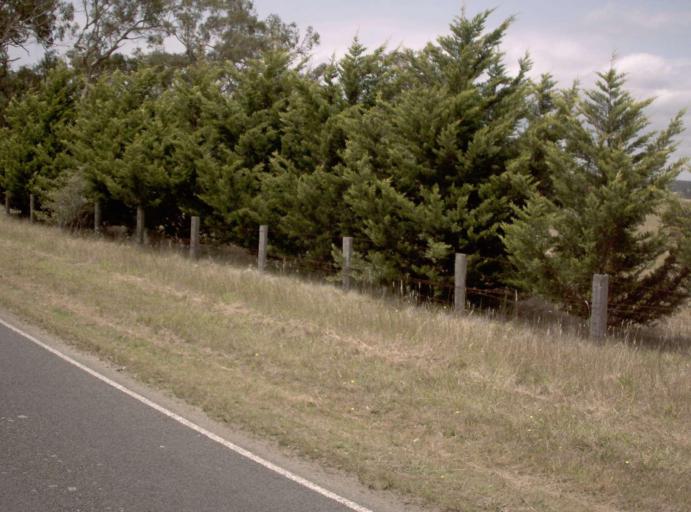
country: AU
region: Victoria
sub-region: Latrobe
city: Traralgon
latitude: -38.5371
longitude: 146.6574
